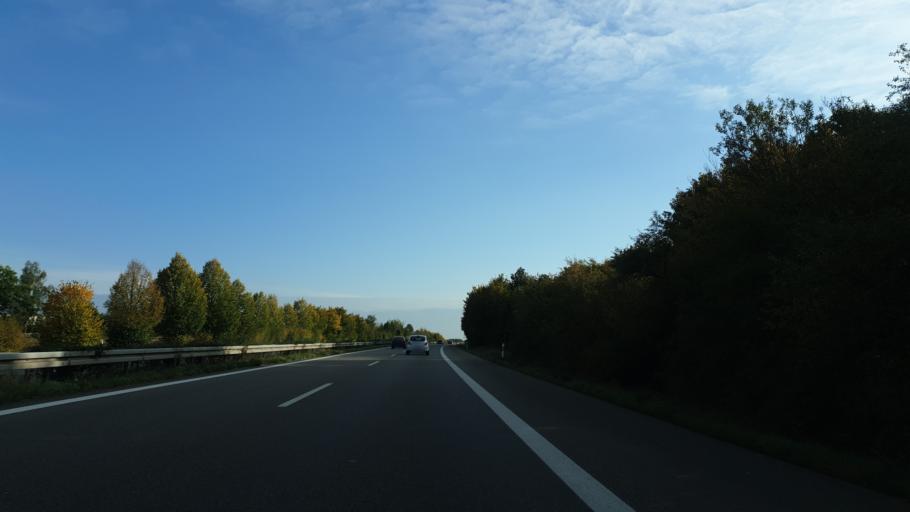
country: DE
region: Saxony
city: Meerane
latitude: 50.8374
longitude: 12.4440
